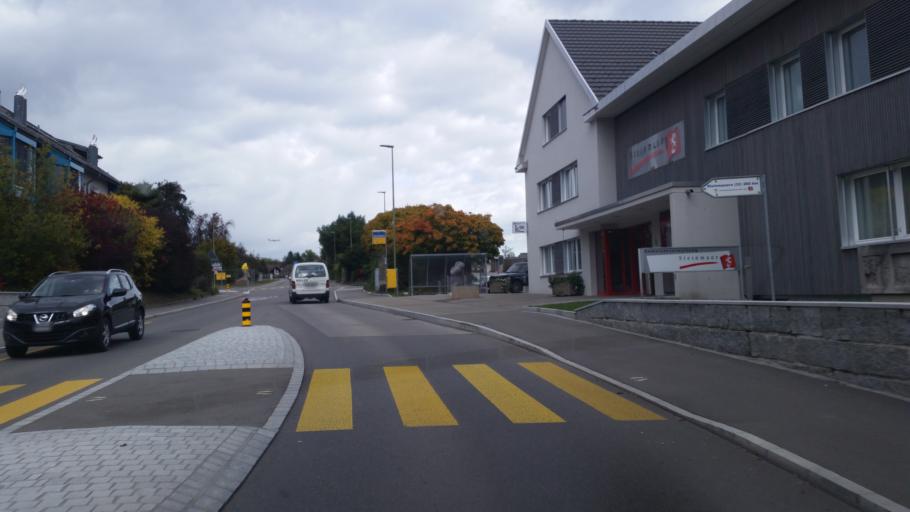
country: CH
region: Zurich
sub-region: Bezirk Dielsdorf
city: Steinmaur
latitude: 47.4939
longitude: 8.4489
